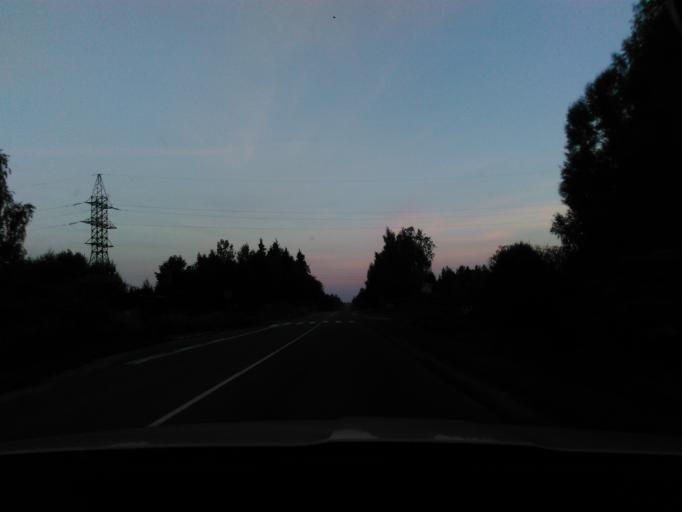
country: RU
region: Moskovskaya
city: Klin
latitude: 56.2422
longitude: 36.7557
